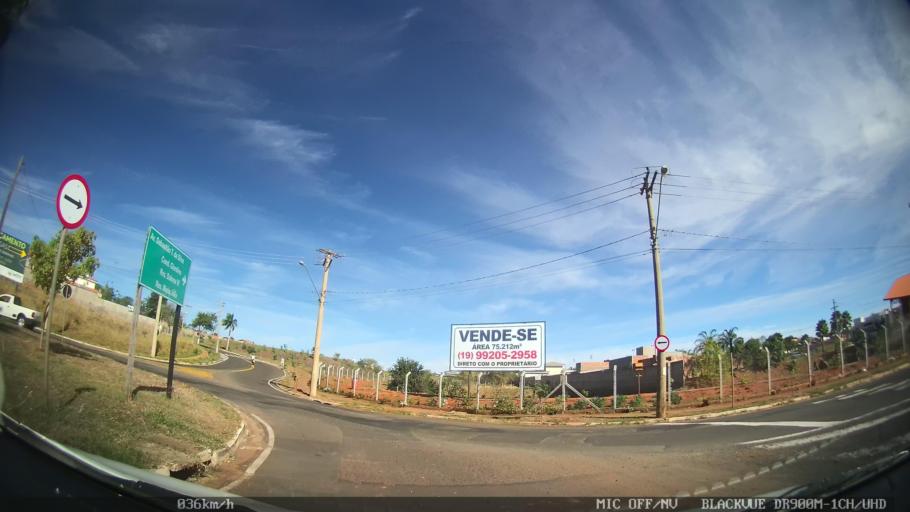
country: BR
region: Sao Paulo
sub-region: Sao Jose Do Rio Preto
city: Sao Jose do Rio Preto
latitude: -20.8004
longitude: -49.3334
